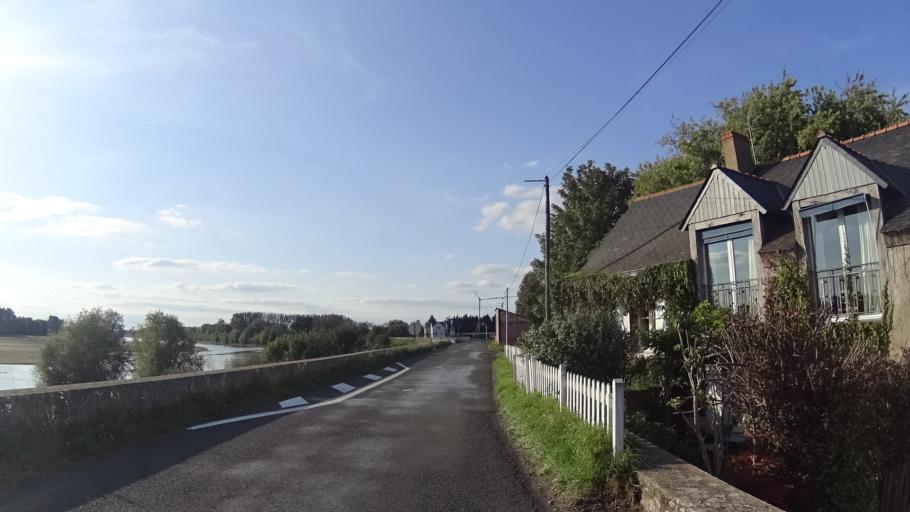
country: FR
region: Pays de la Loire
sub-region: Departement de Maine-et-Loire
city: Saint-Germain-des-Pres
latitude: 47.3928
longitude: -0.8377
